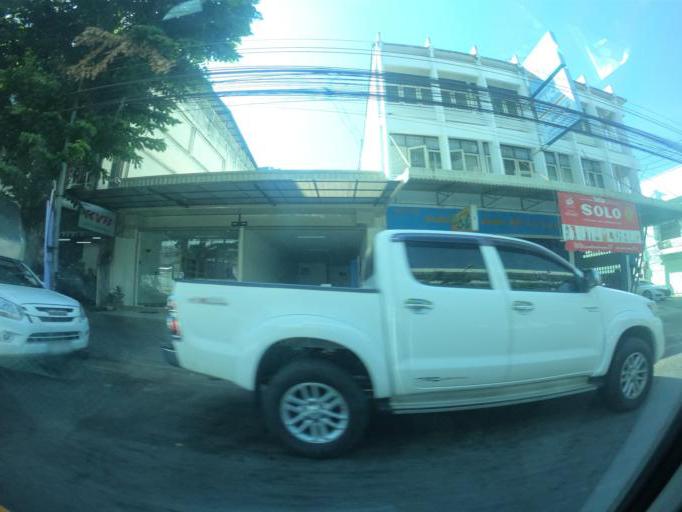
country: TH
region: Khon Kaen
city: Sam Sung
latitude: 16.4937
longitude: 102.9643
